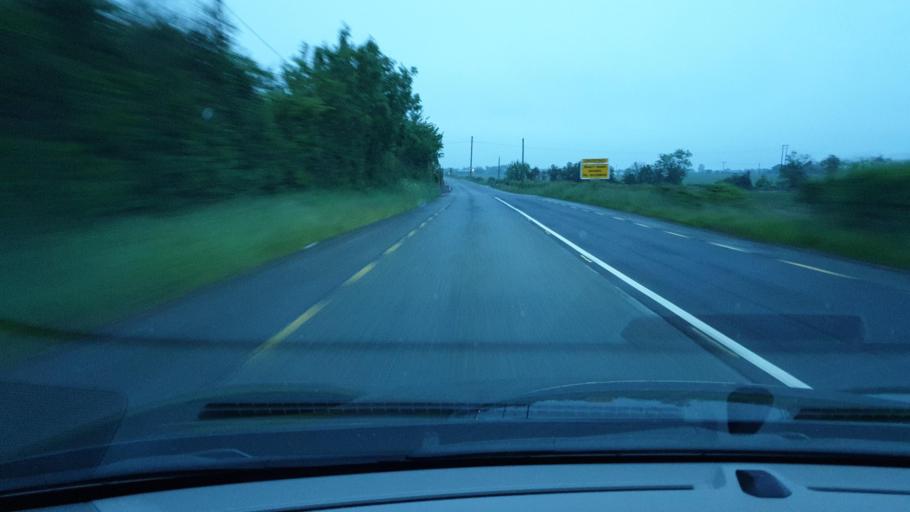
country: IE
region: Leinster
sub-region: Fingal County
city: Blanchardstown
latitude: 53.4483
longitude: -6.3435
